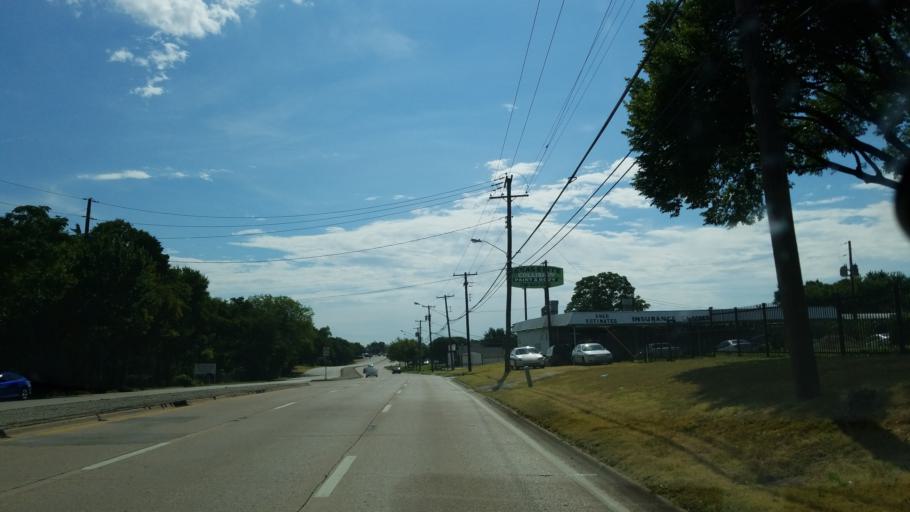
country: US
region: Texas
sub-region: Dallas County
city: Cockrell Hill
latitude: 32.6911
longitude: -96.8856
